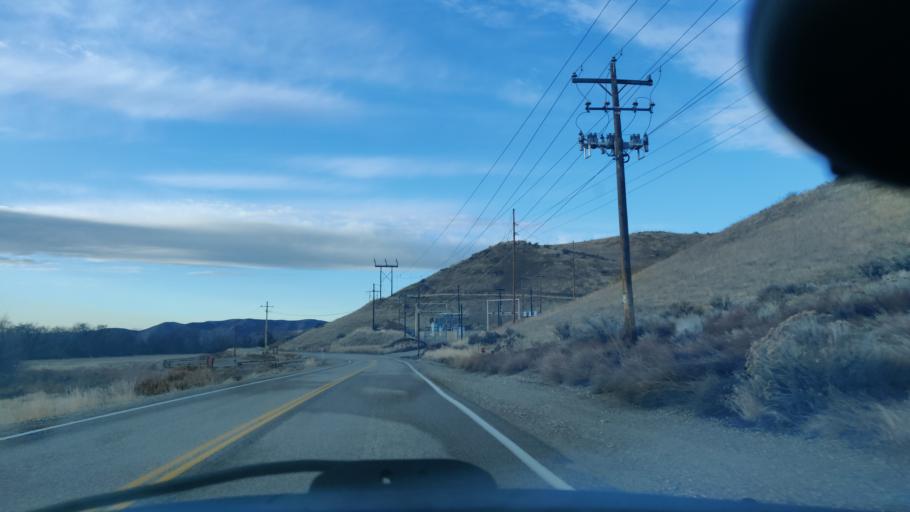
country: US
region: Idaho
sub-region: Ada County
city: Garden City
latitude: 43.7247
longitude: -116.2464
